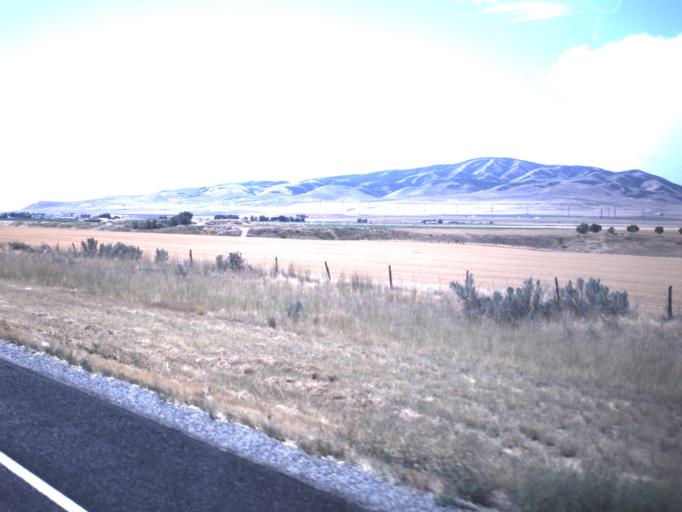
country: US
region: Utah
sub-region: Box Elder County
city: Garland
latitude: 41.8494
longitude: -112.1463
